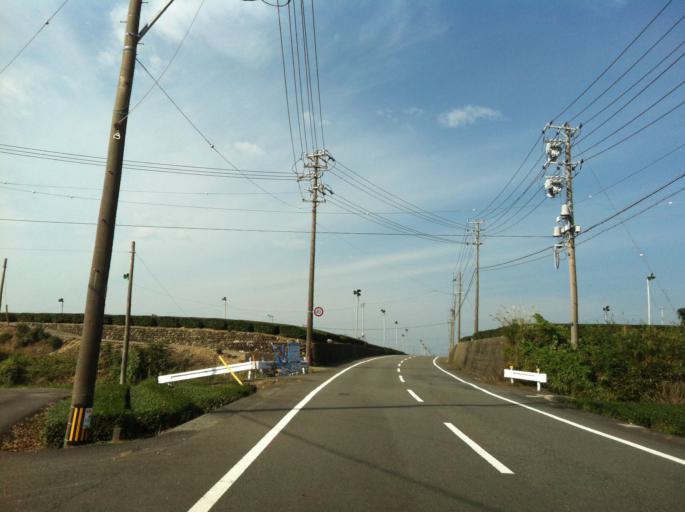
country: JP
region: Shizuoka
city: Shimada
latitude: 34.7725
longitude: 138.1542
